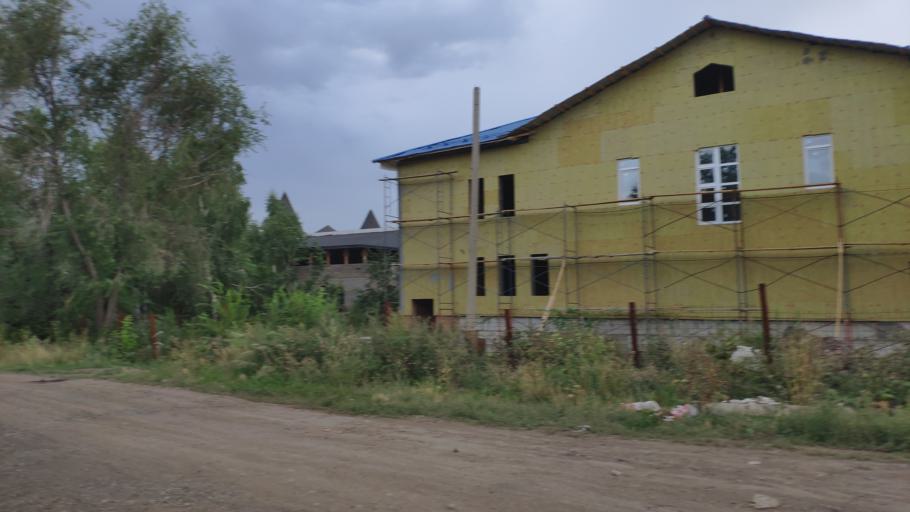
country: RU
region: Chelyabinsk
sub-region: Gorod Magnitogorsk
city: Magnitogorsk
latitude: 53.4143
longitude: 59.0021
